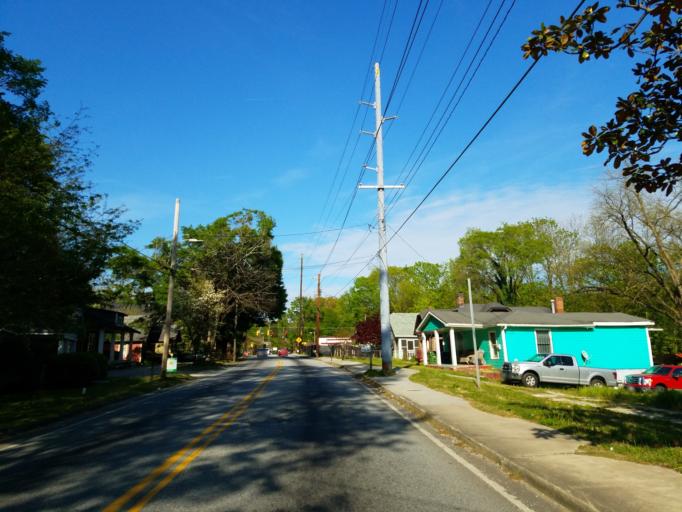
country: US
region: Georgia
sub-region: Cobb County
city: Vinings
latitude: 33.8117
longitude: -84.4740
